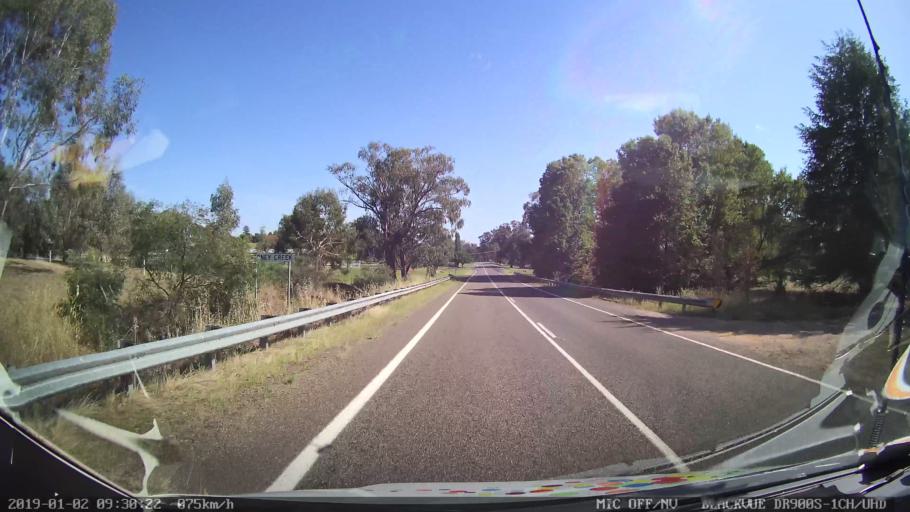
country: AU
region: New South Wales
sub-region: Tumut Shire
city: Tumut
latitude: -35.3275
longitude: 148.2376
